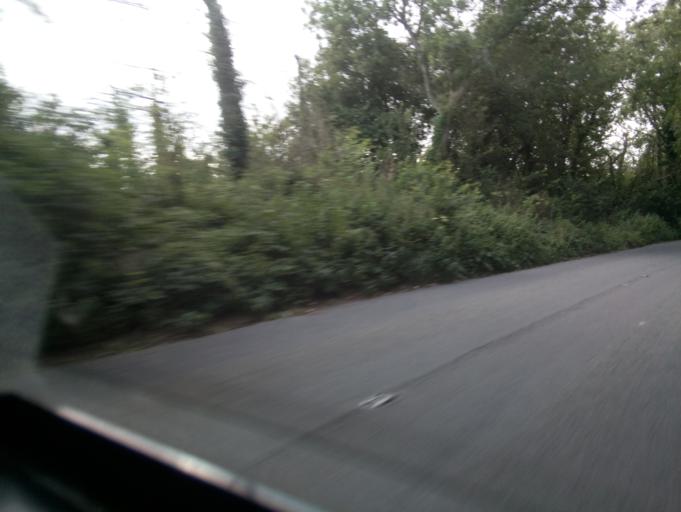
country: GB
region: England
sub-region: Gloucestershire
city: Chipping Campden
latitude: 52.0050
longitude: -1.7610
